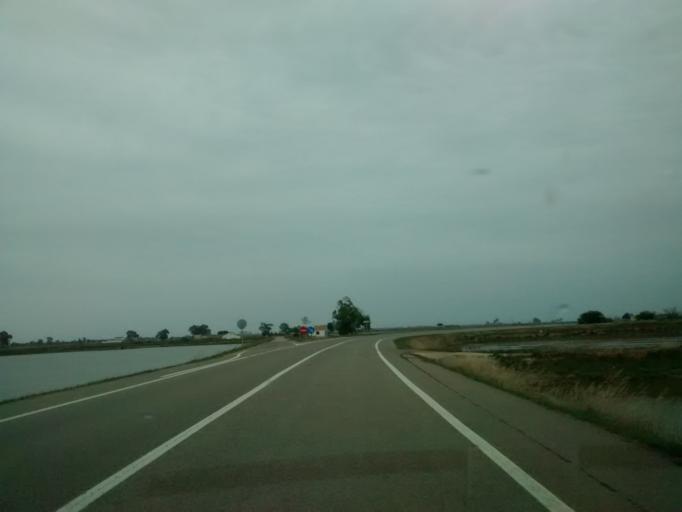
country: ES
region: Catalonia
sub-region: Provincia de Tarragona
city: Deltebre
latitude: 40.7007
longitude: 0.6760
